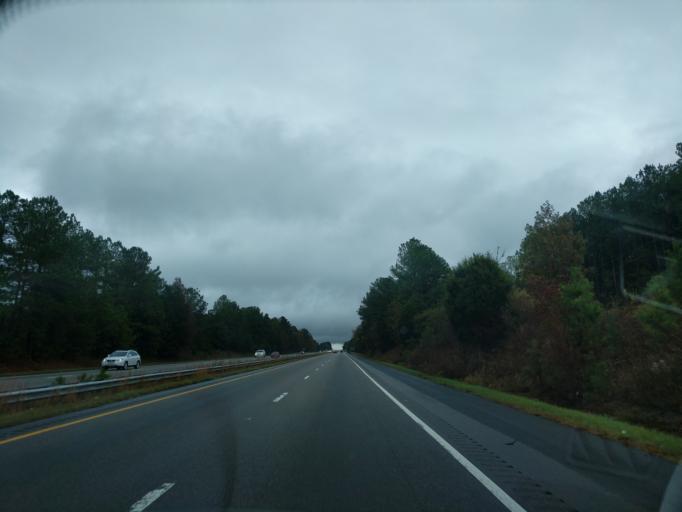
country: US
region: North Carolina
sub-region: Durham County
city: Gorman
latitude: 36.0414
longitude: -78.8226
